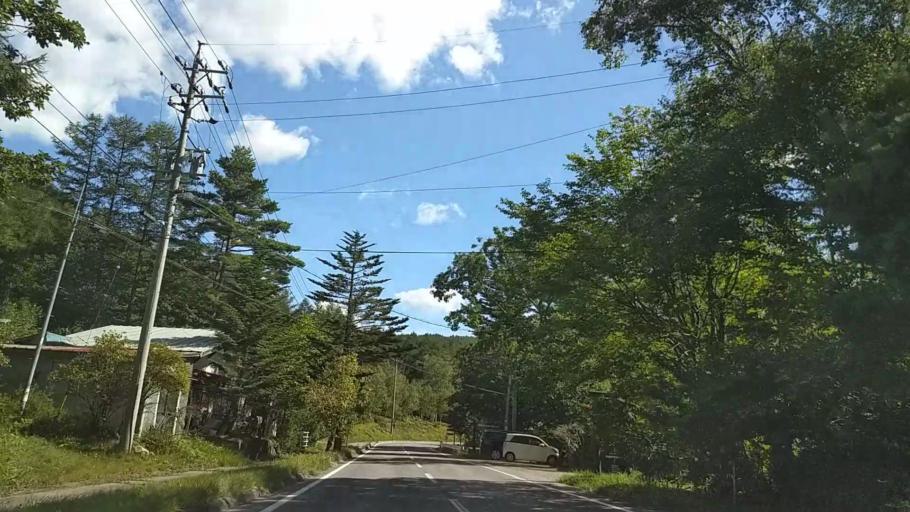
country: JP
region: Nagano
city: Chino
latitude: 36.1150
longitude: 138.2607
